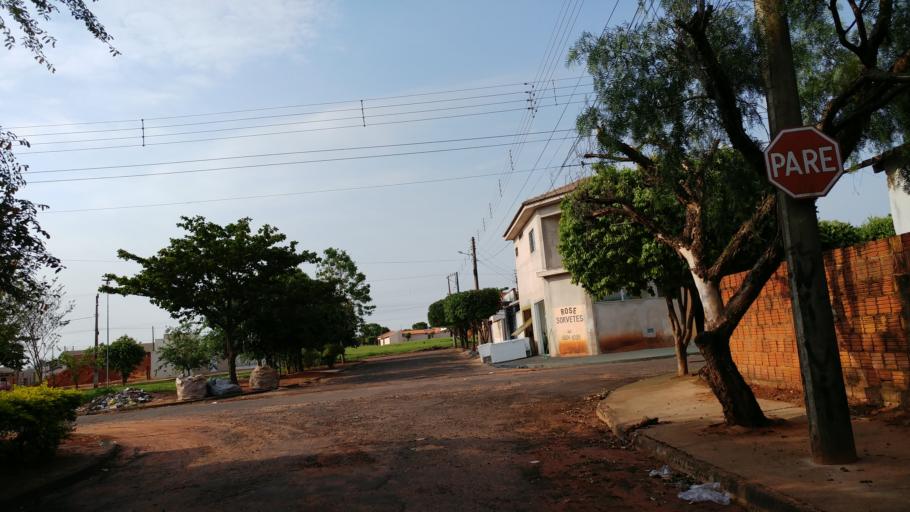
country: BR
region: Sao Paulo
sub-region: Paraguacu Paulista
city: Paraguacu Paulista
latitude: -22.4184
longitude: -50.5897
